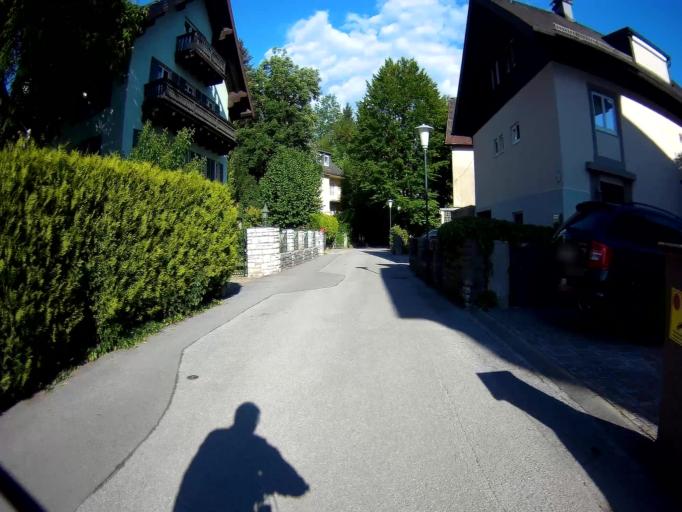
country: AT
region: Salzburg
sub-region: Salzburg Stadt
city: Salzburg
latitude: 47.7944
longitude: 13.0683
